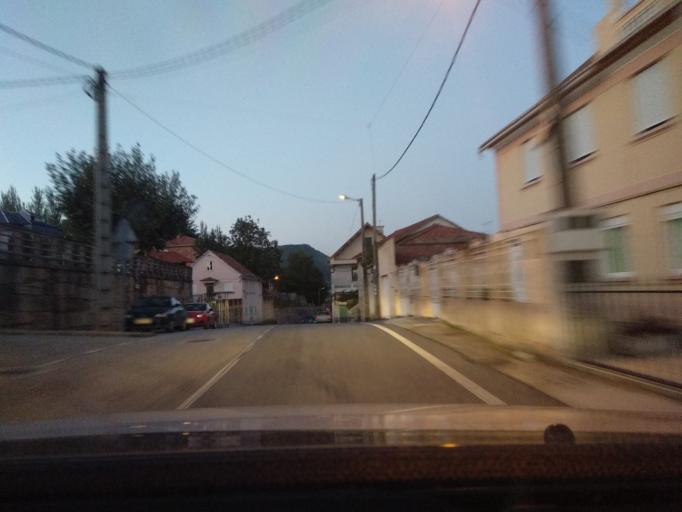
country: ES
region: Galicia
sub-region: Provincia de Pontevedra
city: Moana
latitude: 42.2826
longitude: -8.7437
